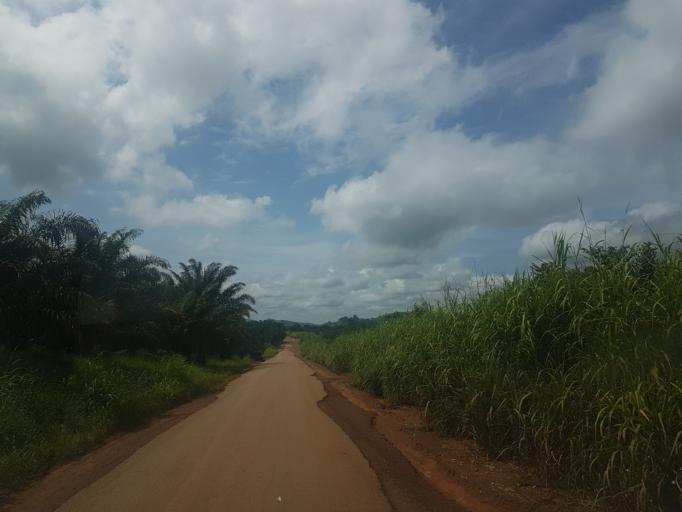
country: GN
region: Nzerekore
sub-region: Prefecture de Guekedou
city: Gueckedou
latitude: 8.6553
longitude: -10.1270
